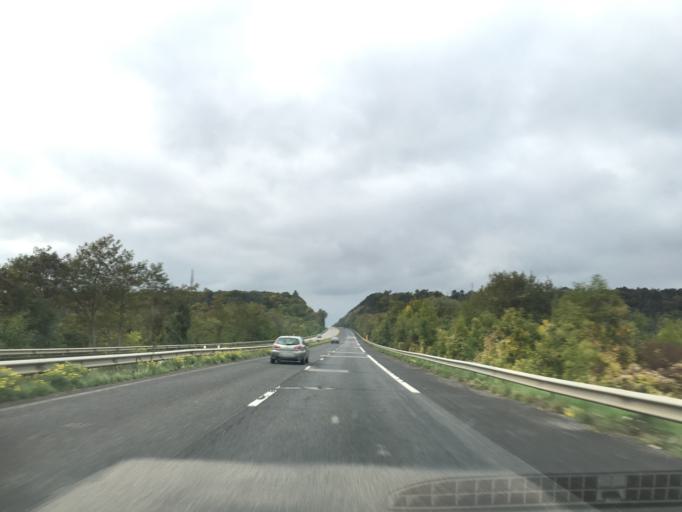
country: FR
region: Lorraine
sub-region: Departement de Meurthe-et-Moselle
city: Foug
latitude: 48.6712
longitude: 5.7797
